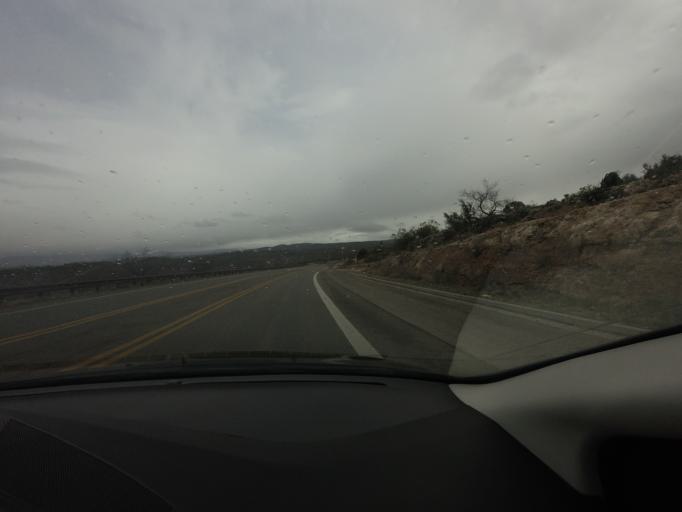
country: US
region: Arizona
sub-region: Yavapai County
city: Lake Montezuma
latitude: 34.6441
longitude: -111.8166
